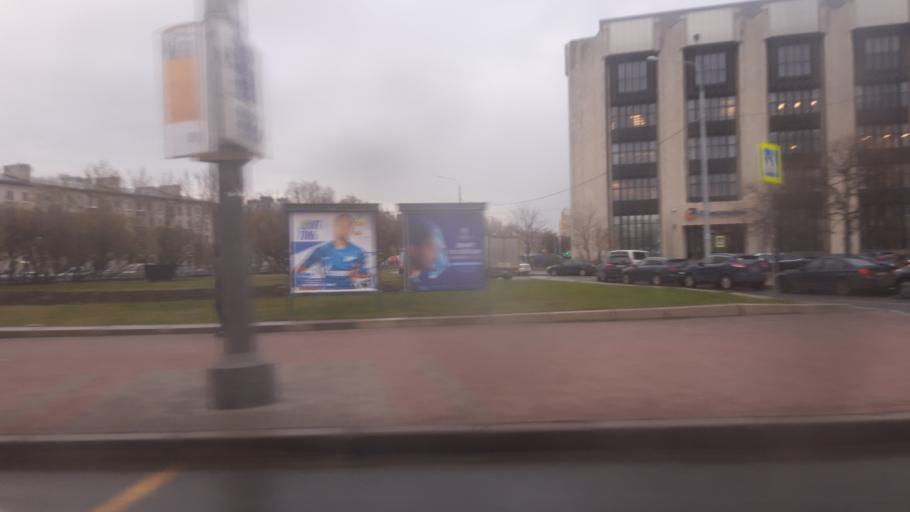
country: RU
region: St.-Petersburg
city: Kupchino
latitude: 59.8437
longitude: 30.3234
